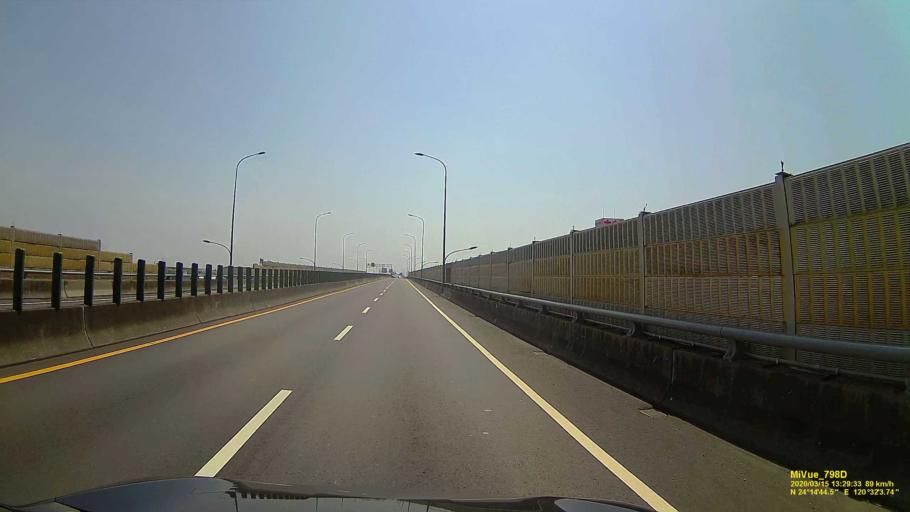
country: TW
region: Taiwan
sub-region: Changhua
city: Chang-hua
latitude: 24.2468
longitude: 120.5347
